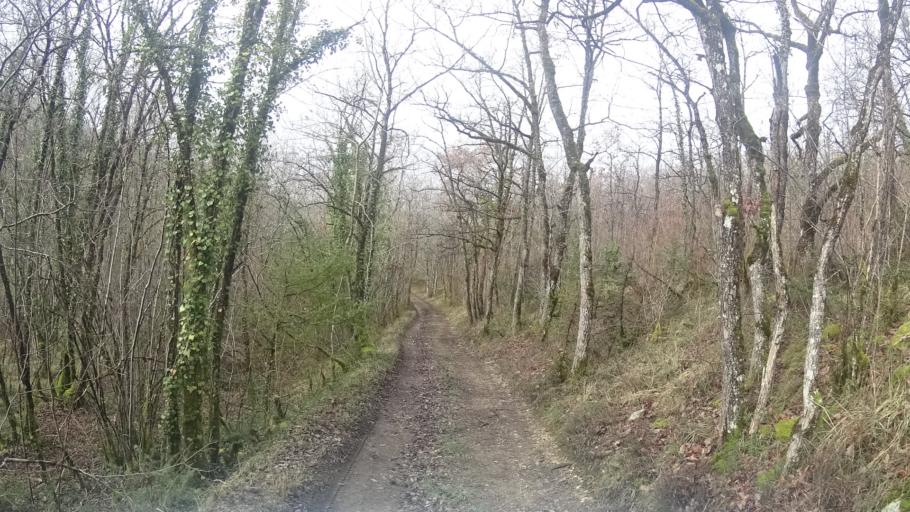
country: FR
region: Aquitaine
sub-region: Departement de la Dordogne
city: Terrasson-Lavilledieu
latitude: 45.1056
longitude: 1.2596
